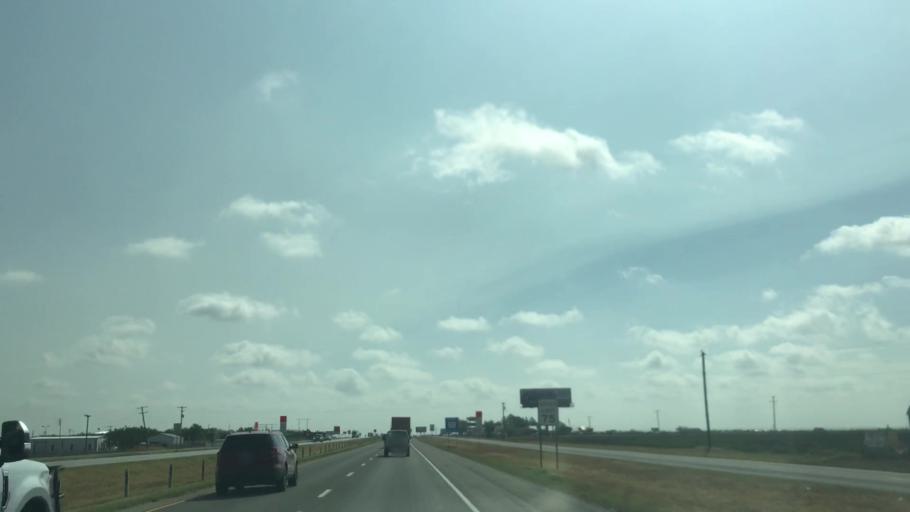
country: US
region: Texas
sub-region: Nolan County
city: Roscoe
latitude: 32.4495
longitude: -100.4887
